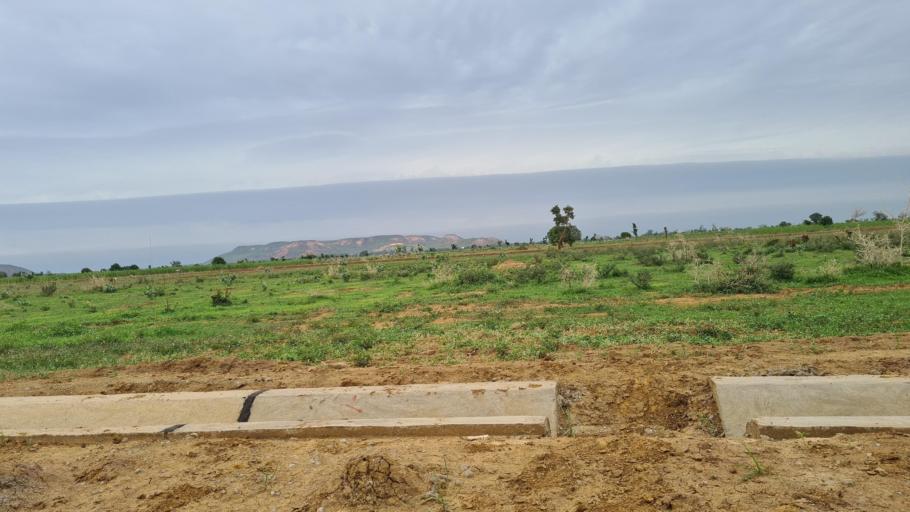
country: NE
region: Tahoua
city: Birni N Konni
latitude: 13.8309
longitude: 5.2648
